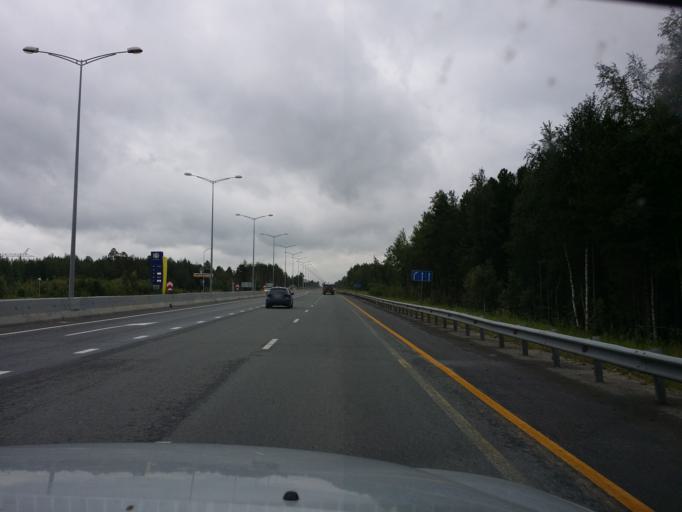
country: RU
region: Khanty-Mansiyskiy Avtonomnyy Okrug
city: Nizhnevartovsk
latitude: 61.0071
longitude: 76.4074
